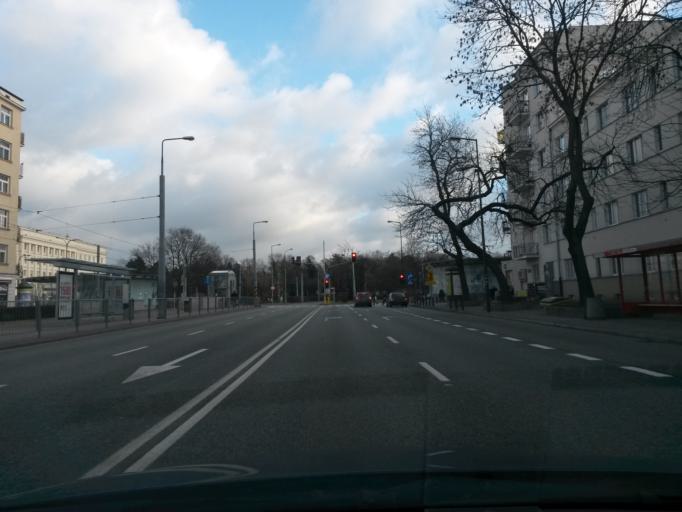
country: PL
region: Masovian Voivodeship
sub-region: Warszawa
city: Zoliborz
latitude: 52.2693
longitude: 20.9843
